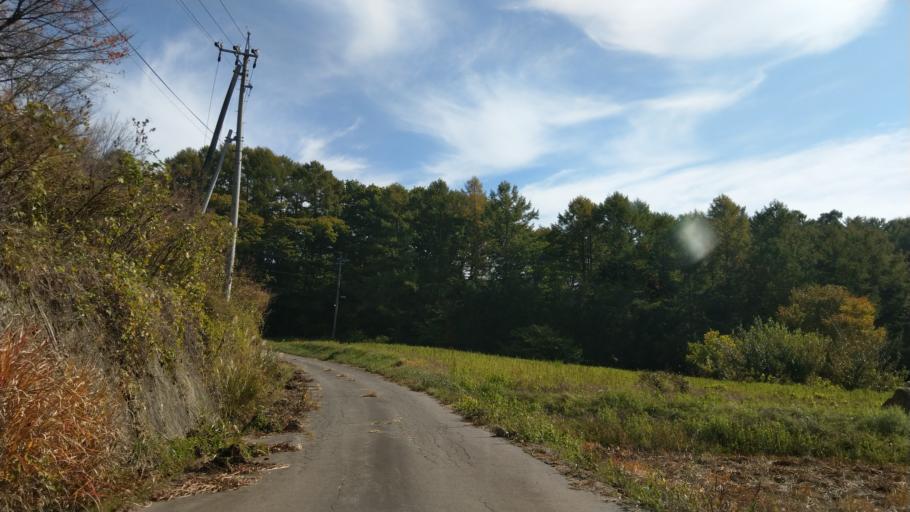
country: JP
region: Nagano
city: Komoro
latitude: 36.3543
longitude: 138.4455
